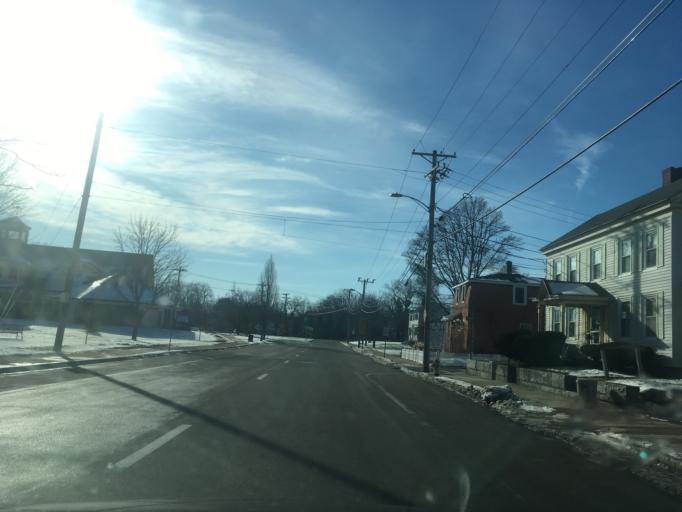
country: US
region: Massachusetts
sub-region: Essex County
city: Salisbury
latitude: 42.8407
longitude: -70.8613
